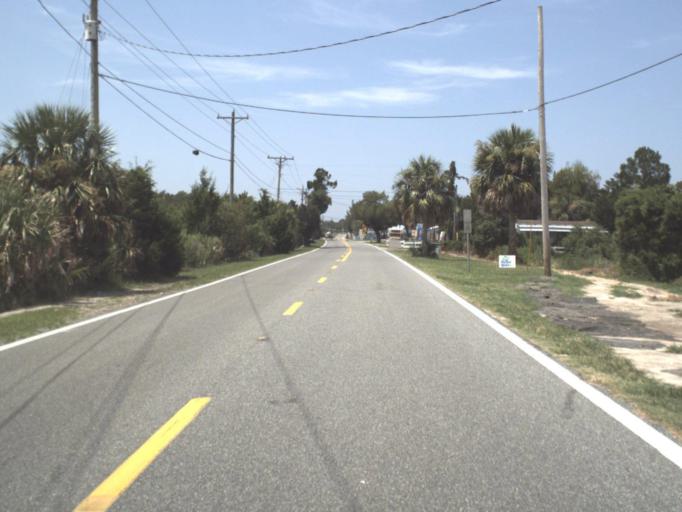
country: US
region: Florida
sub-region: Levy County
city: Chiefland
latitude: 29.1566
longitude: -83.0298
